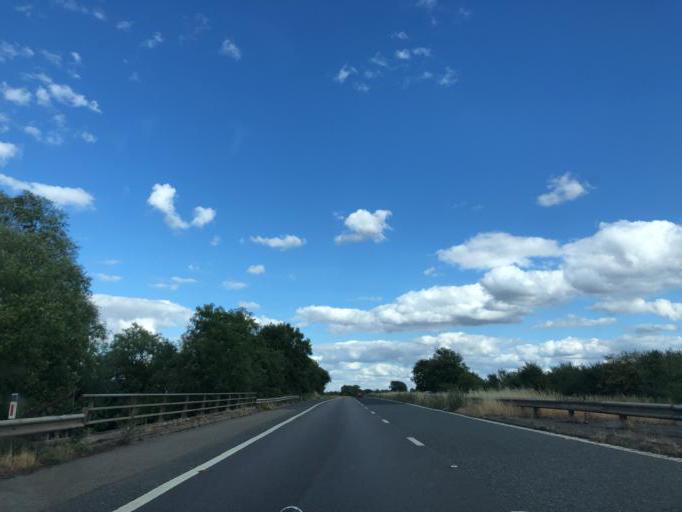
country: GB
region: England
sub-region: Warwickshire
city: Rugby
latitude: 52.3382
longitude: -1.2259
